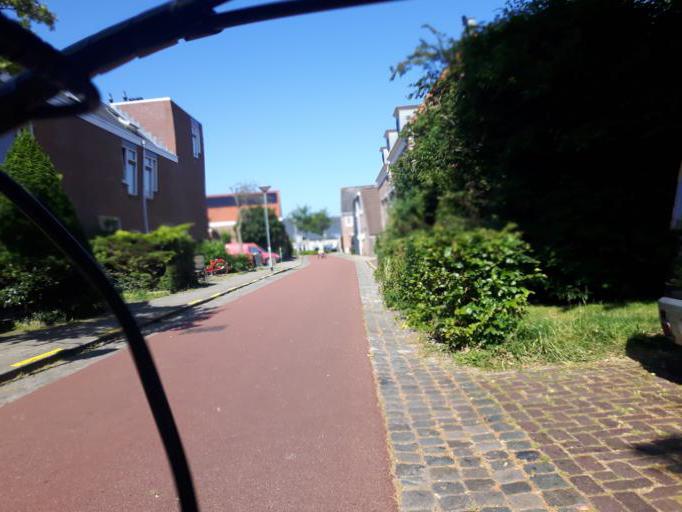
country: NL
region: Zeeland
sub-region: Gemeente Middelburg
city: Middelburg
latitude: 51.4950
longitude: 3.6233
